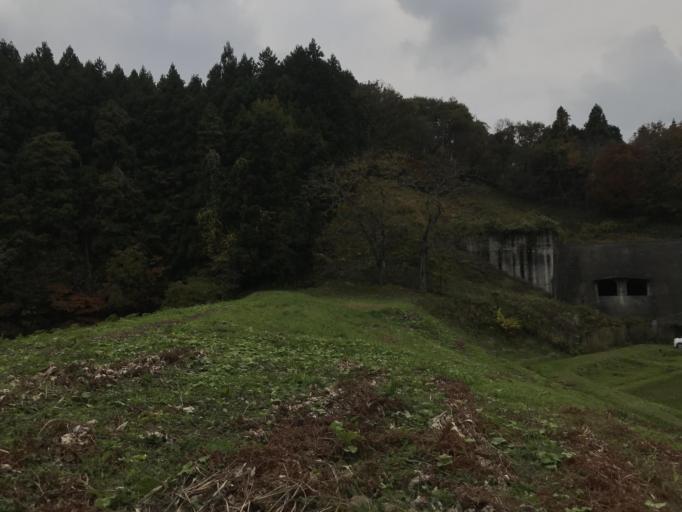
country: JP
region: Iwate
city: Ichinoseki
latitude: 38.8917
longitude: 141.1274
